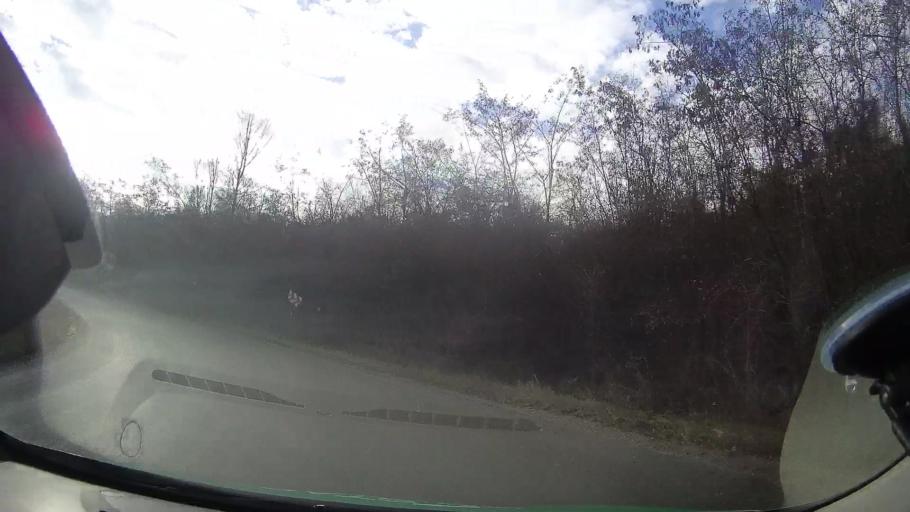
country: RO
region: Cluj
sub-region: Comuna Savadisla
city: Savadisla
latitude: 46.6570
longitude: 23.4519
